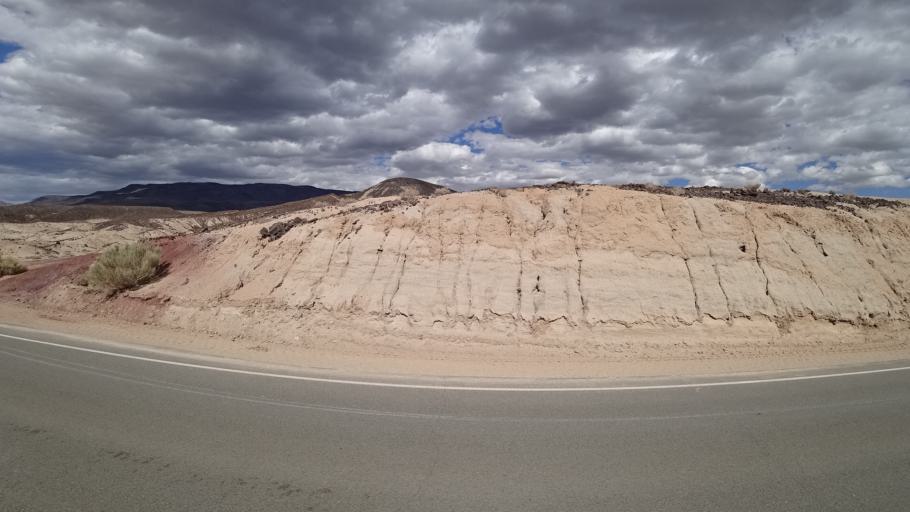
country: US
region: California
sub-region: Inyo County
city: Lone Pine
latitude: 36.3790
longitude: -117.8033
